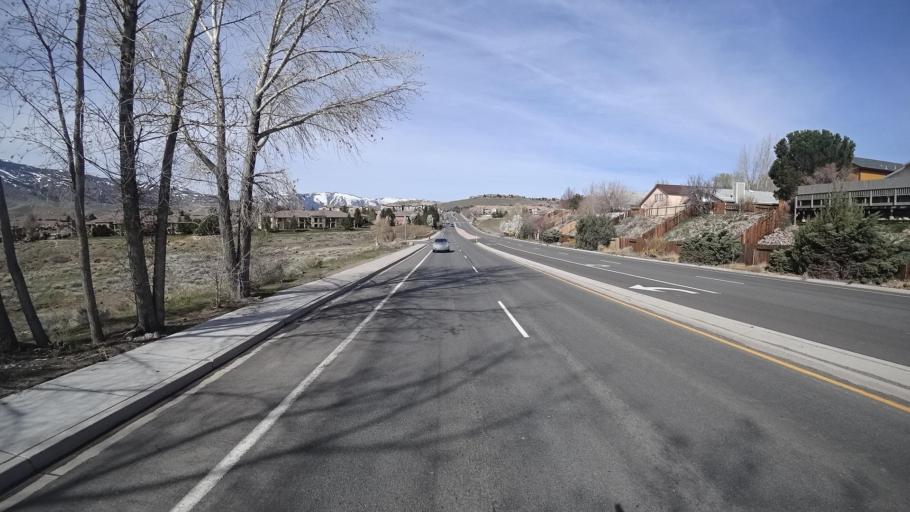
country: US
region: Nevada
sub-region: Washoe County
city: Mogul
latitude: 39.5190
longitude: -119.8935
